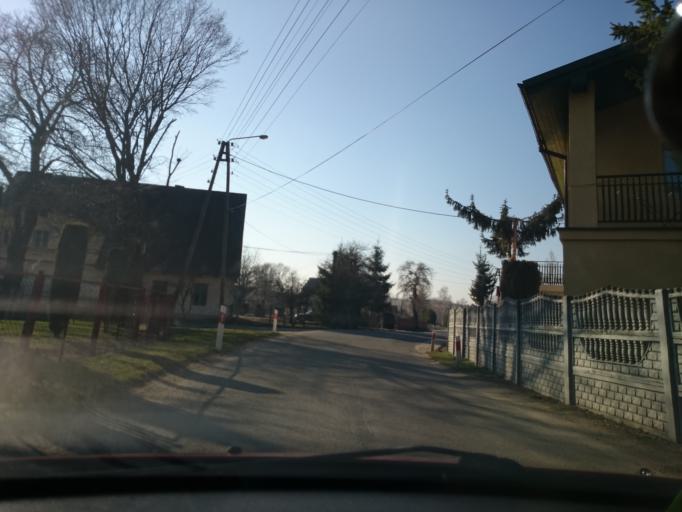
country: PL
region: Lower Silesian Voivodeship
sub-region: Powiat klodzki
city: Klodzko
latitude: 50.3819
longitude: 16.6331
